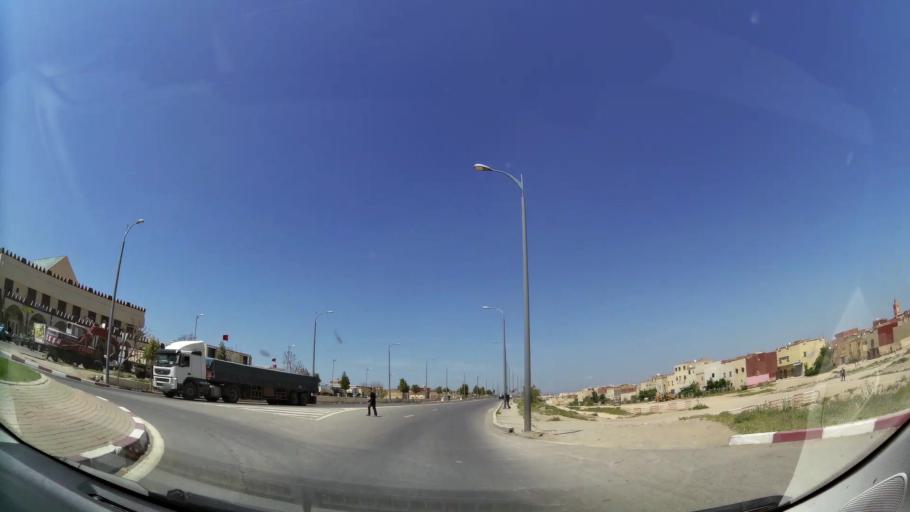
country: MA
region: Oriental
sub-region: Oujda-Angad
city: Oujda
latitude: 34.6904
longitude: -1.9437
